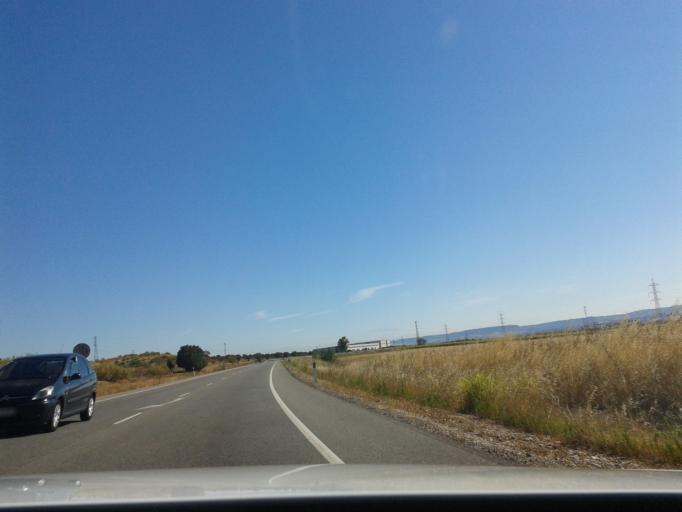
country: ES
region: Castille-La Mancha
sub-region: Provincia de Guadalajara
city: Quer
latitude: 40.5880
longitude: -3.2709
